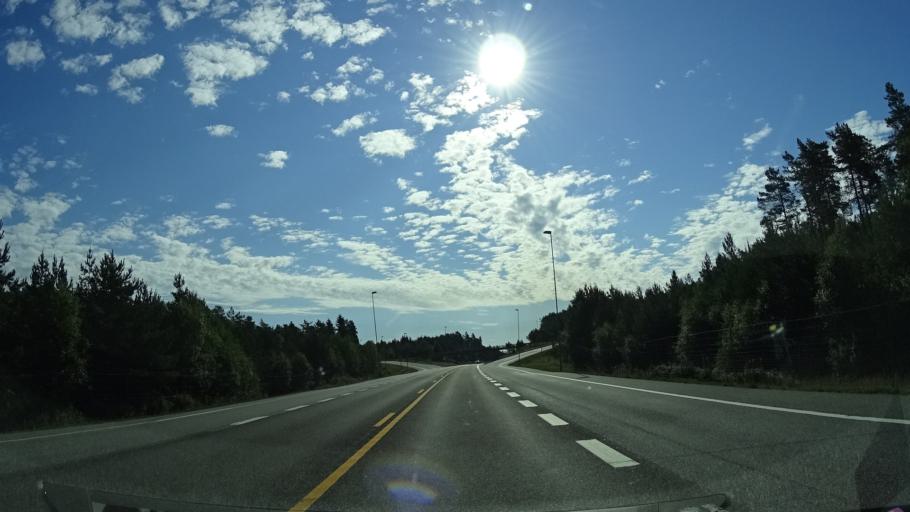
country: NO
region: Ostfold
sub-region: Marker
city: Orje
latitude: 59.5400
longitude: 11.5331
